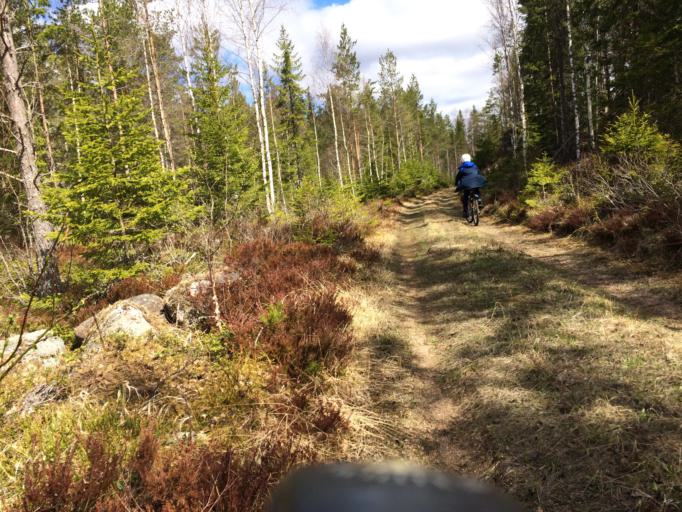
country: SE
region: OErebro
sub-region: Hallefors Kommun
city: Haellefors
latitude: 60.0434
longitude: 14.5256
